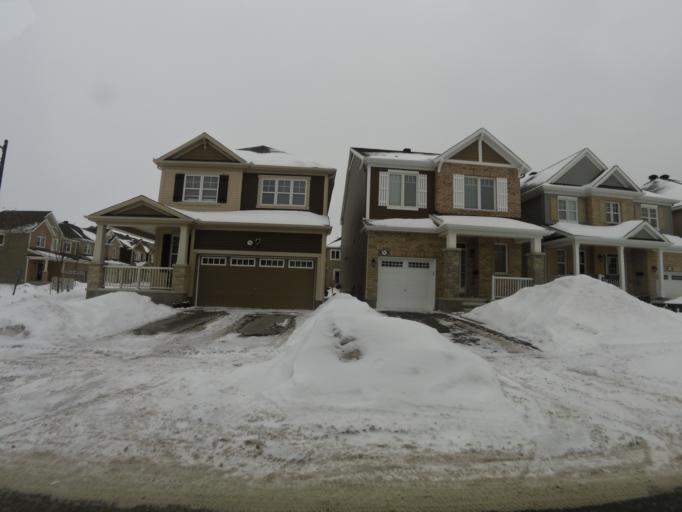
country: CA
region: Ontario
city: Bells Corners
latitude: 45.2816
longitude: -75.9252
